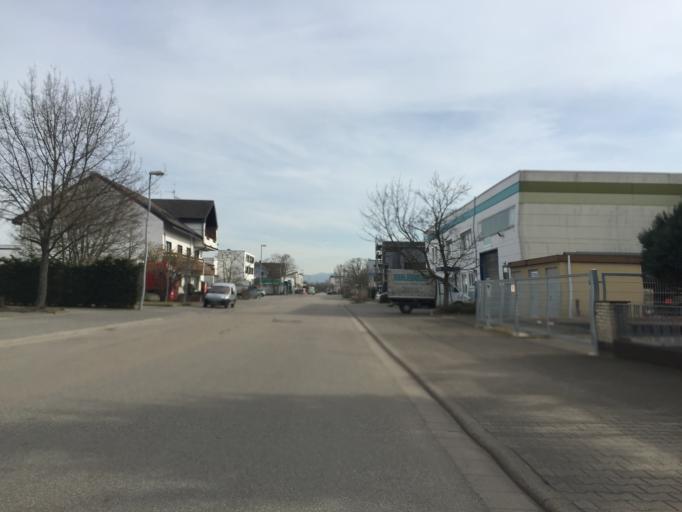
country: DE
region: Hesse
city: Viernheim
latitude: 49.5530
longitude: 8.5934
